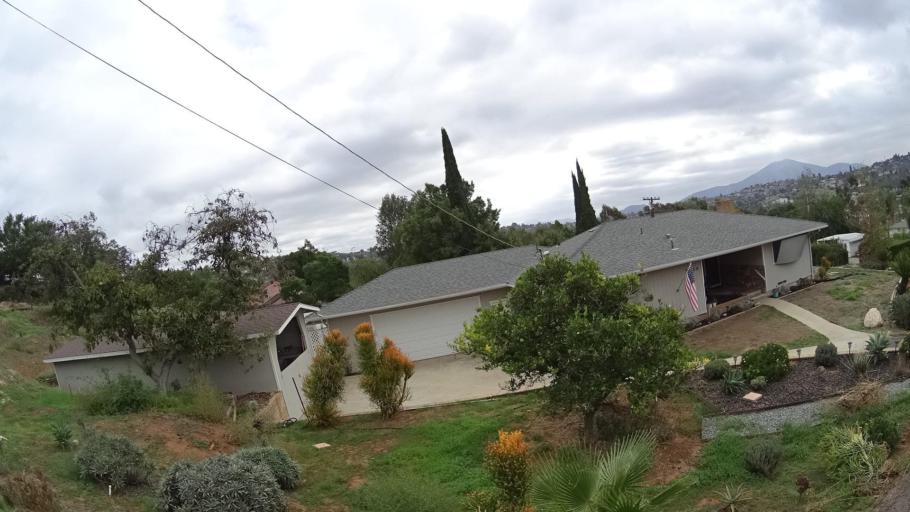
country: US
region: California
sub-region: San Diego County
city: Spring Valley
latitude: 32.7520
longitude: -116.9914
